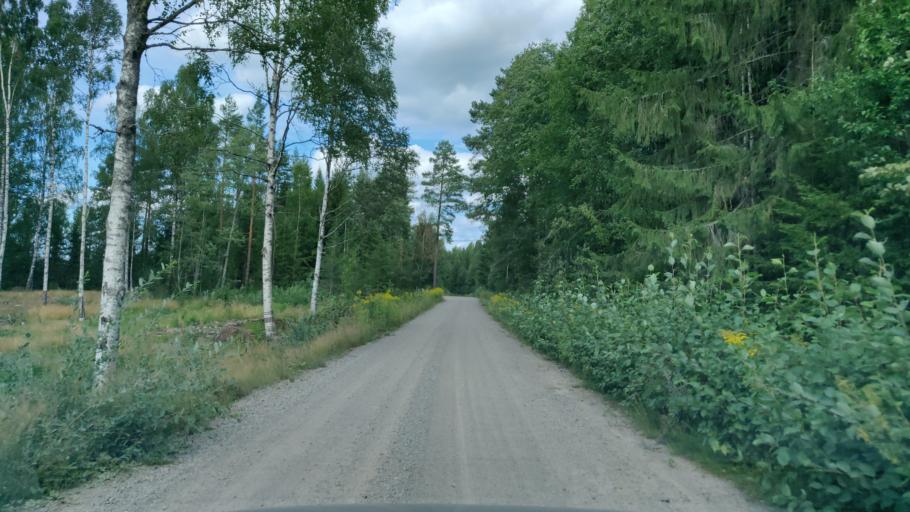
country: SE
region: Vaermland
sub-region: Hagfors Kommun
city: Hagfors
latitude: 60.0107
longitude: 13.6944
